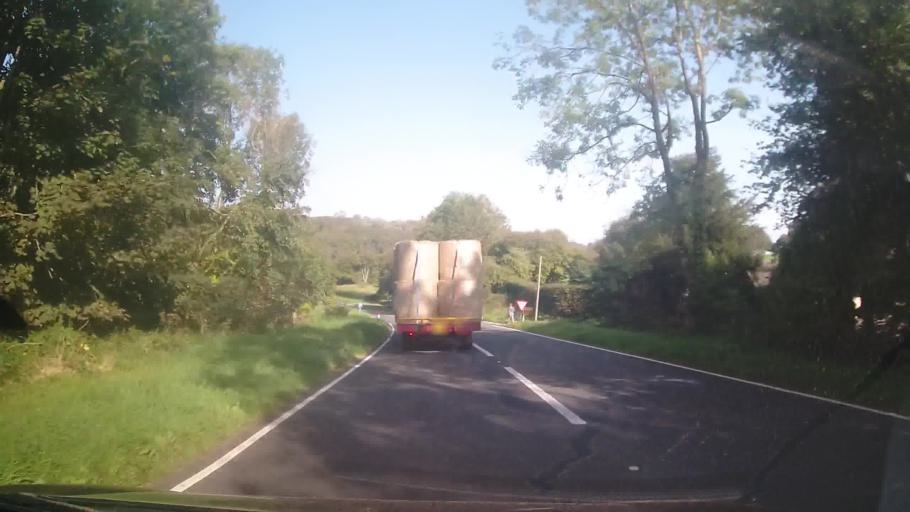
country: GB
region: Wales
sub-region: Pembrokeshire
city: Nevern
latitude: 52.0139
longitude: -4.7739
